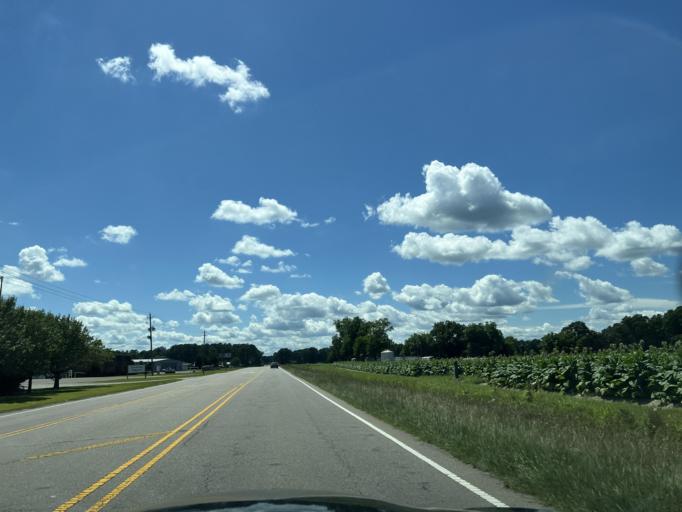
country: US
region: North Carolina
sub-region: Lee County
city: Sanford
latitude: 35.4376
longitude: -79.1979
